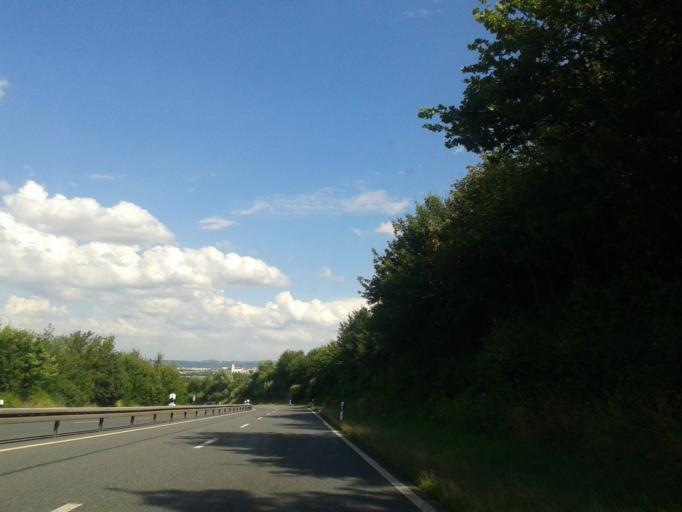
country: DE
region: Saxony
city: Radebeul
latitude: 51.0729
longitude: 13.6586
